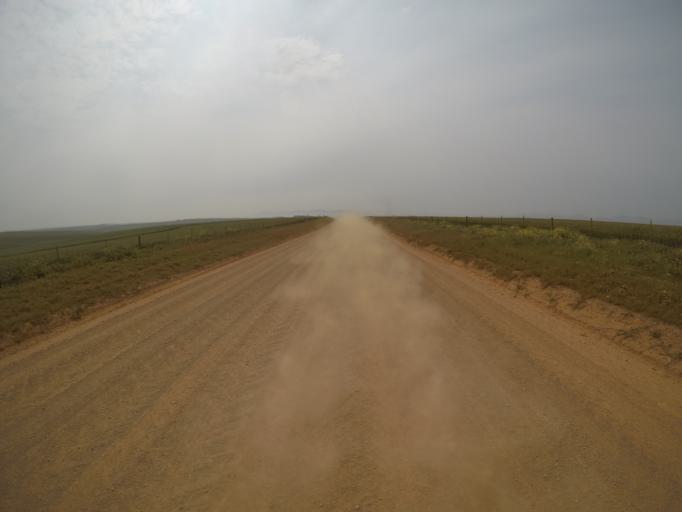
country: ZA
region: Western Cape
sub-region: City of Cape Town
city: Kraaifontein
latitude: -33.7163
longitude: 18.6819
